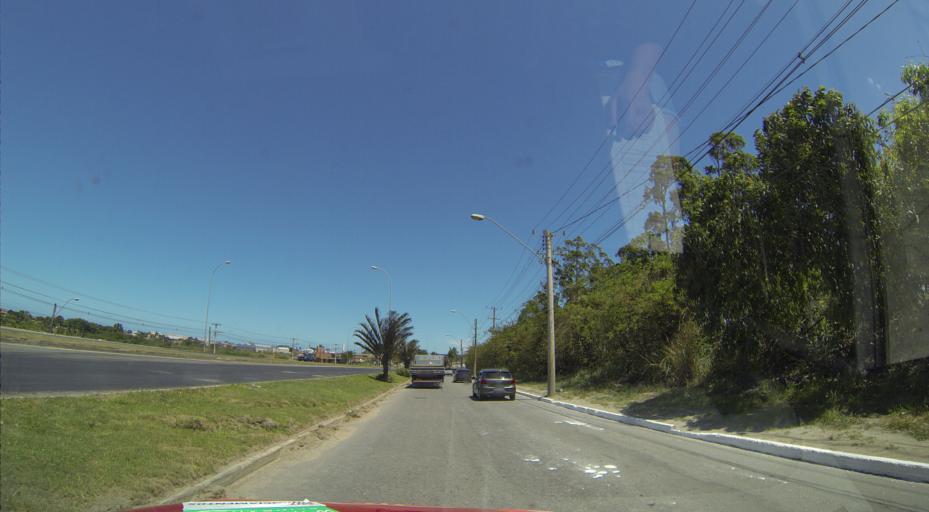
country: BR
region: Espirito Santo
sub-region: Serra
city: Serra
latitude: -20.1742
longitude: -40.2670
